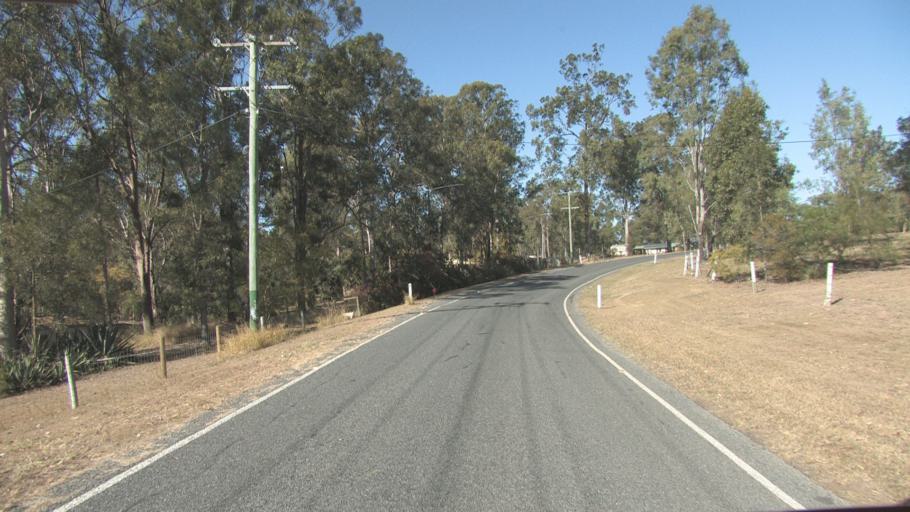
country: AU
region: Queensland
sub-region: Logan
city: Cedar Vale
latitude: -27.8758
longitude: 152.9849
